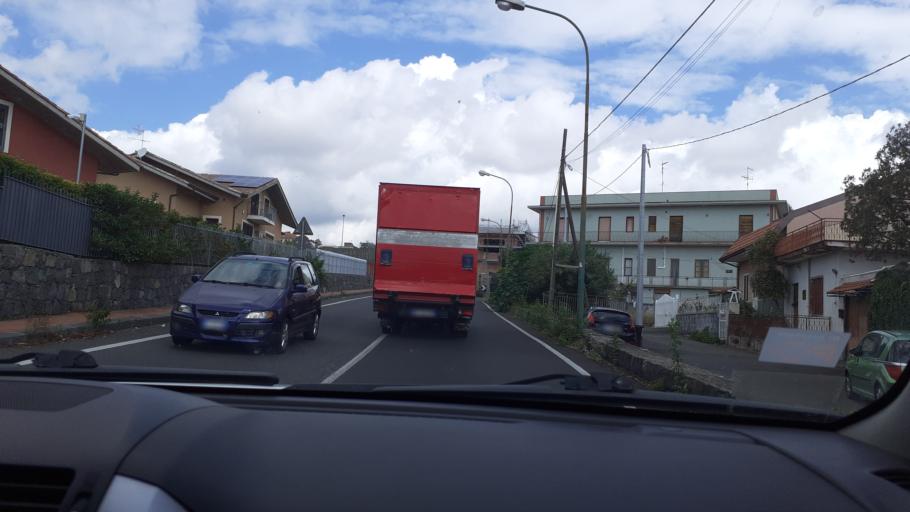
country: IT
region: Sicily
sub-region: Catania
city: Cerza
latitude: 37.5487
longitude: 15.1002
